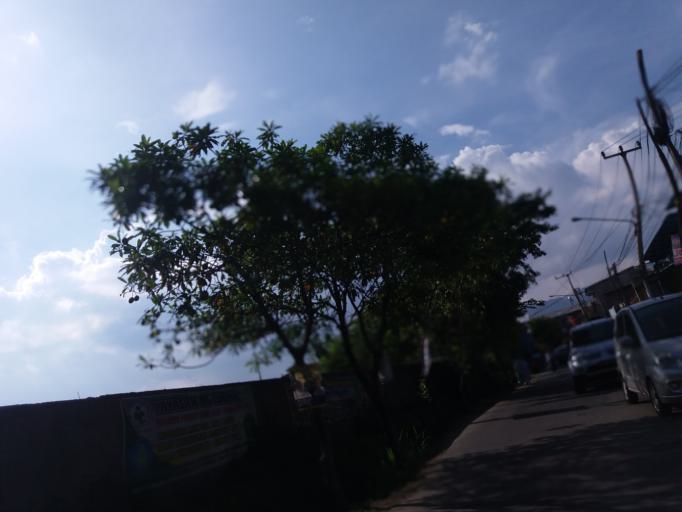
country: ID
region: West Java
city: Bandung
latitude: -6.9210
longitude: 107.6633
